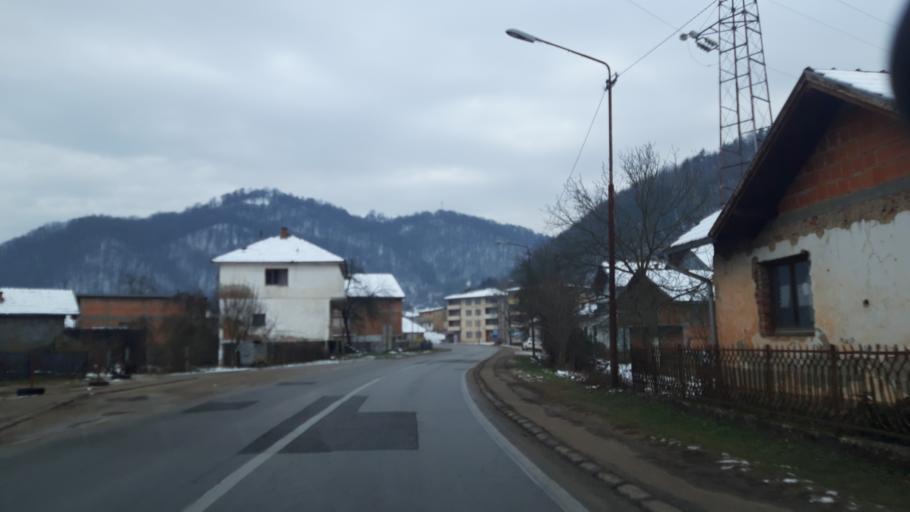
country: BA
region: Republika Srpska
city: Milici
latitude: 44.2153
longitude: 19.1071
